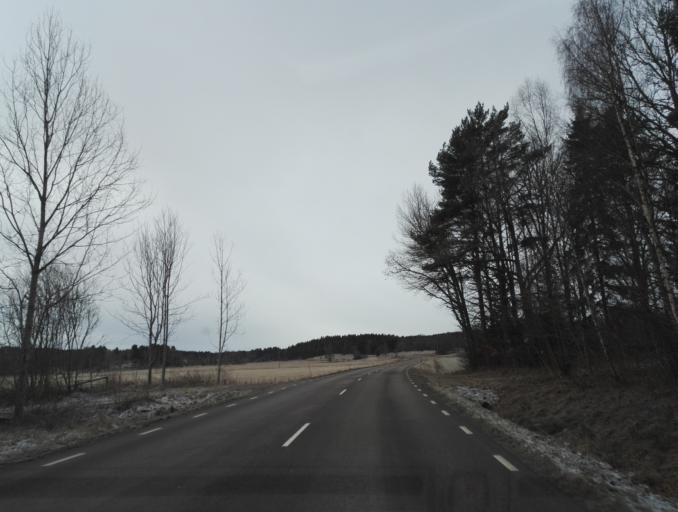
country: SE
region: Kalmar
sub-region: Hultsfreds Kommun
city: Virserum
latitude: 57.3533
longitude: 15.6105
